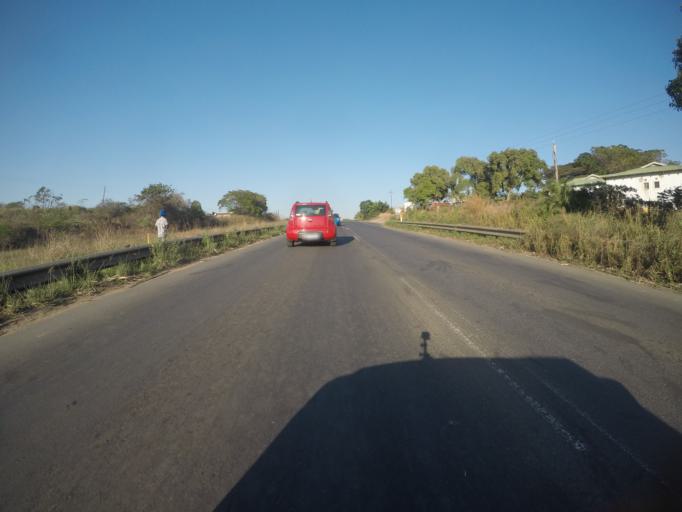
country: ZA
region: KwaZulu-Natal
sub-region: iLembe District Municipality
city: Stanger
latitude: -29.4028
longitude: 31.2510
